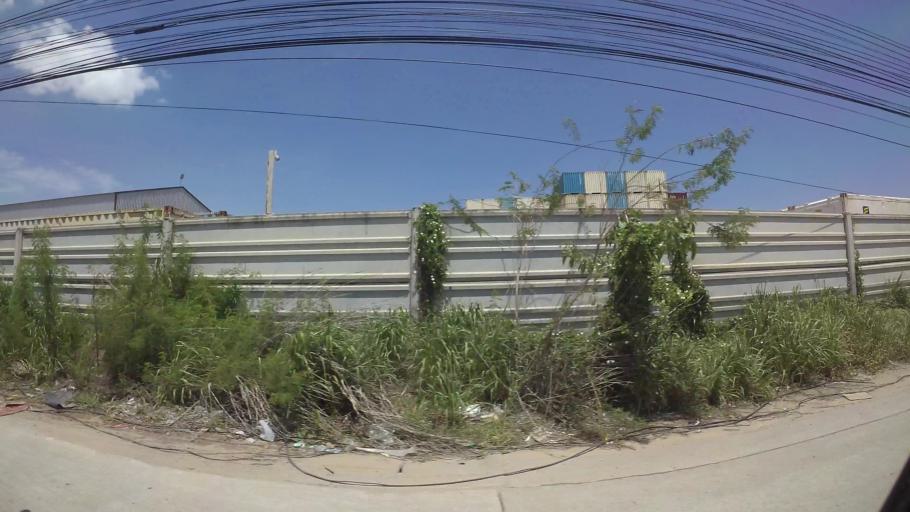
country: TH
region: Chon Buri
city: Si Racha
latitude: 13.1190
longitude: 100.9565
